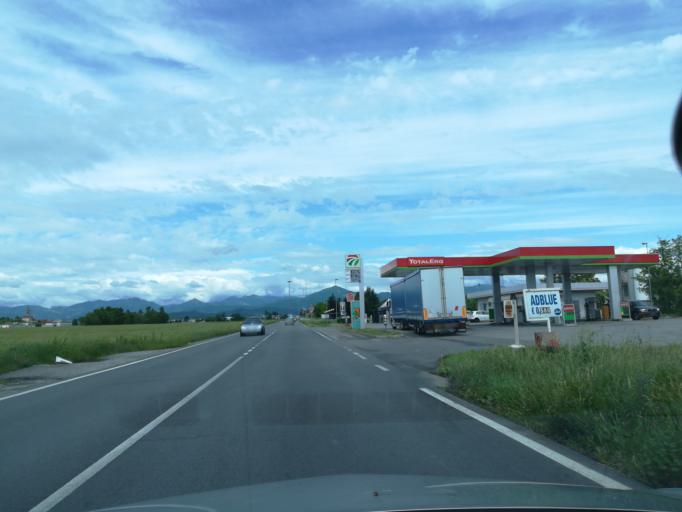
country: IT
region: Lombardy
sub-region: Provincia di Bergamo
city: Mornico al Serio
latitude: 45.6057
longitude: 9.8073
